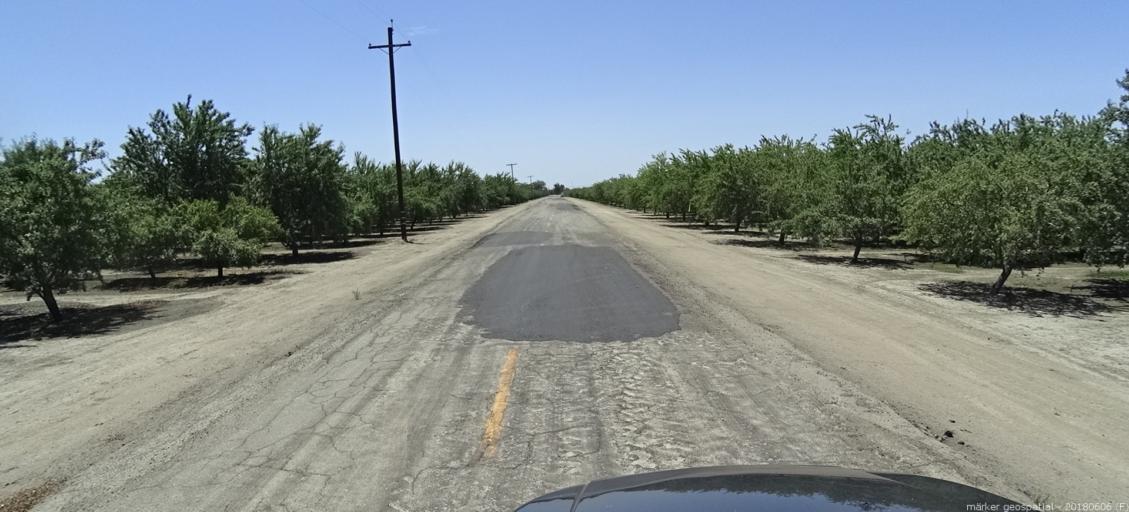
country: US
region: California
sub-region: Fresno County
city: Firebaugh
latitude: 36.8512
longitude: -120.4178
